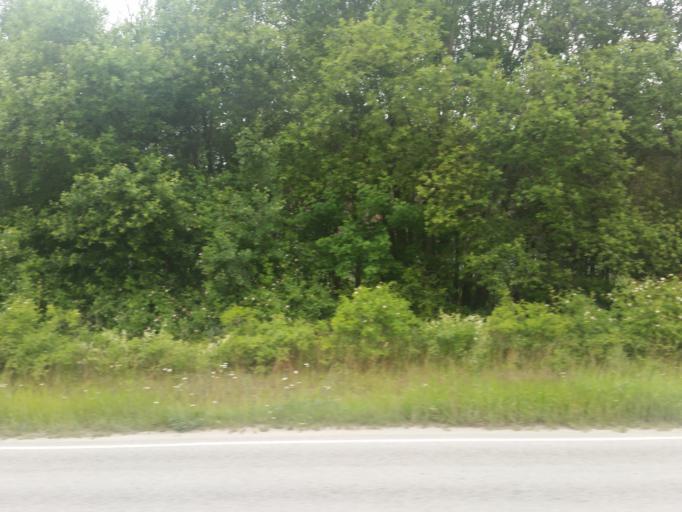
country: SE
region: Stockholm
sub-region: Stockholms Kommun
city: Kista
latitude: 59.4155
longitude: 17.9046
